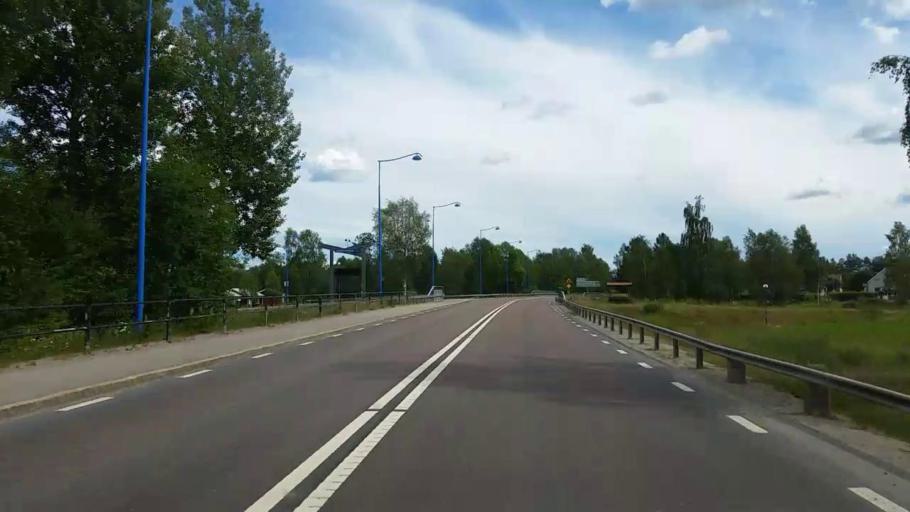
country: SE
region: Gaevleborg
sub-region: Ovanakers Kommun
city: Edsbyn
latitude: 61.3834
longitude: 15.8256
